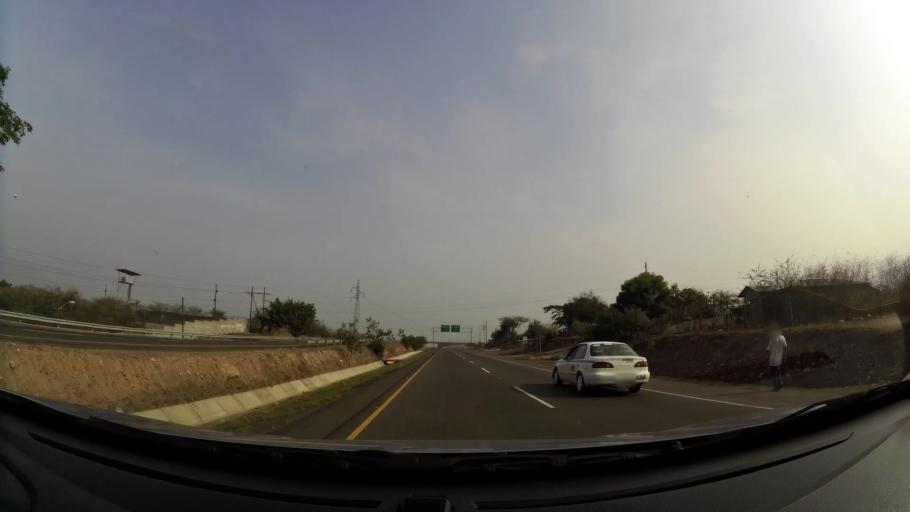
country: HN
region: Comayagua
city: Comayagua
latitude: 14.3974
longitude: -87.6167
